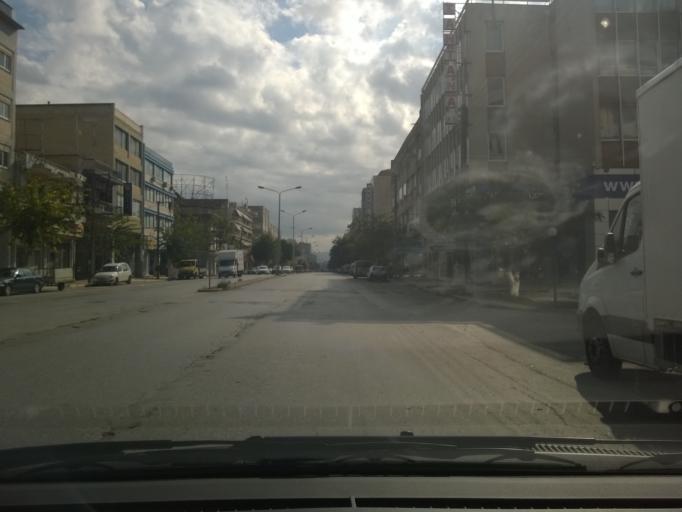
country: GR
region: Central Macedonia
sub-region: Nomos Thessalonikis
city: Ampelokipoi
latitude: 40.6506
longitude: 22.9158
